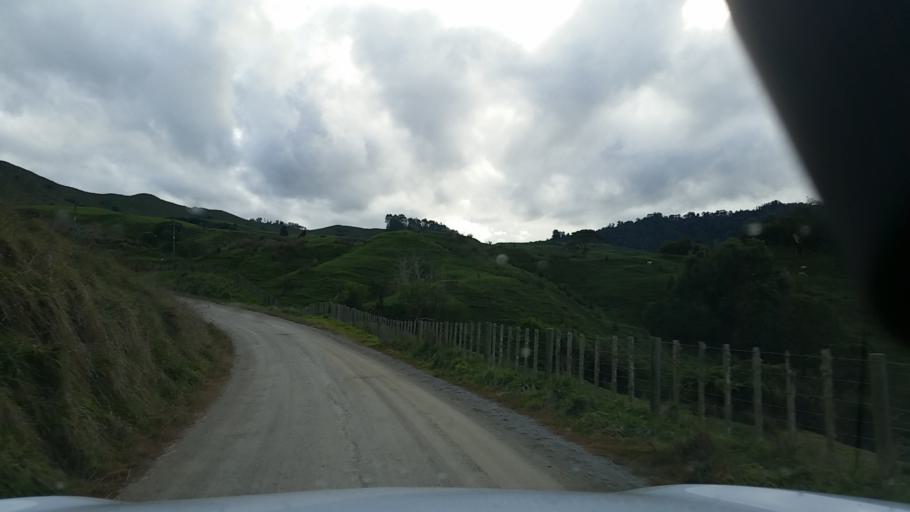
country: NZ
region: Taranaki
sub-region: South Taranaki District
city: Patea
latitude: -39.5546
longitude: 174.7975
